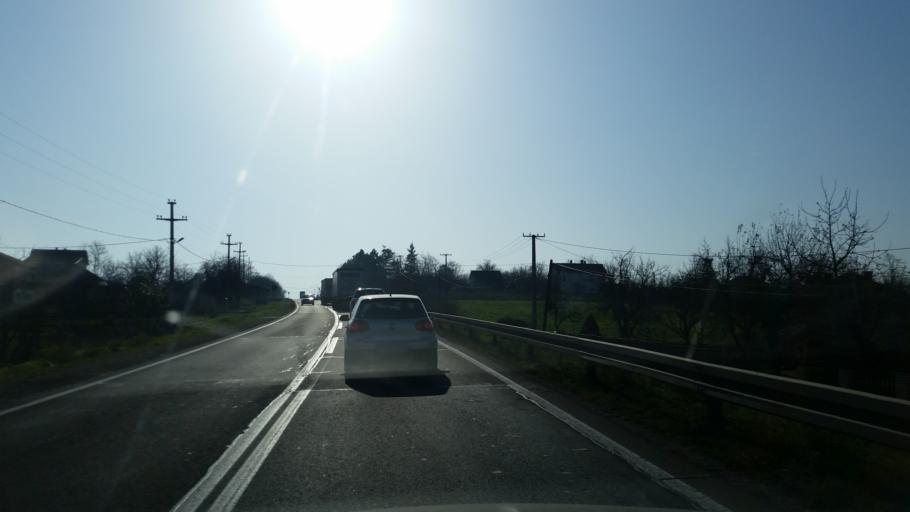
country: RS
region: Central Serbia
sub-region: Kolubarski Okrug
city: Lajkovac
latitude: 44.3571
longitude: 20.1898
